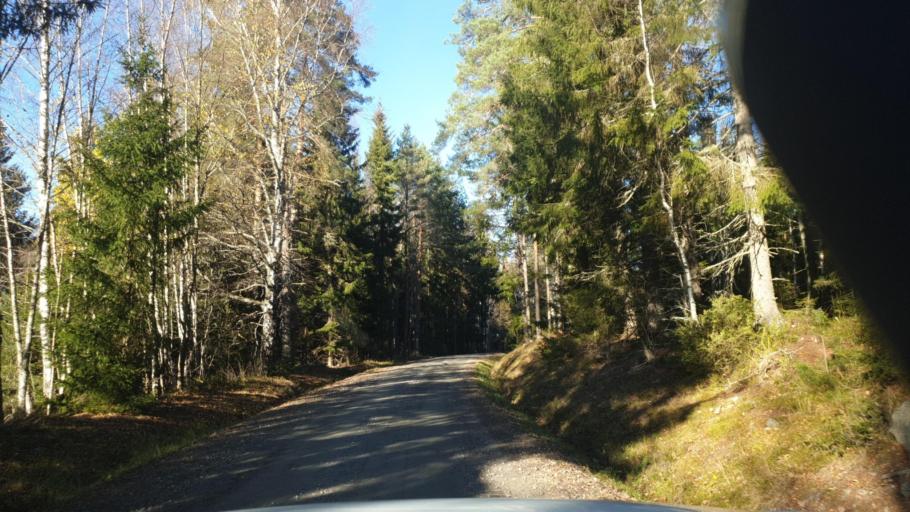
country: SE
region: Vaermland
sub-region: Karlstads Kommun
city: Edsvalla
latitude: 59.5151
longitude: 13.0126
